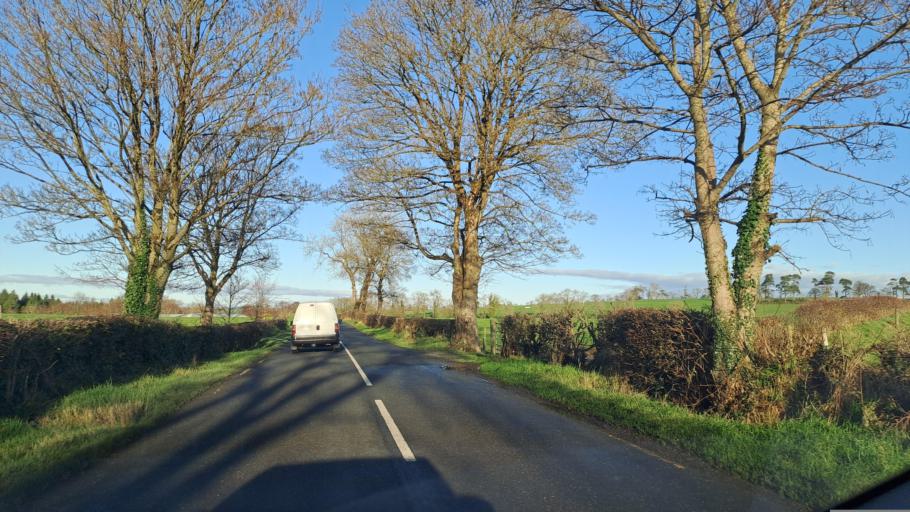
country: IE
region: Ulster
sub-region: An Cabhan
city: Mullagh
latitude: 53.8168
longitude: -6.9494
